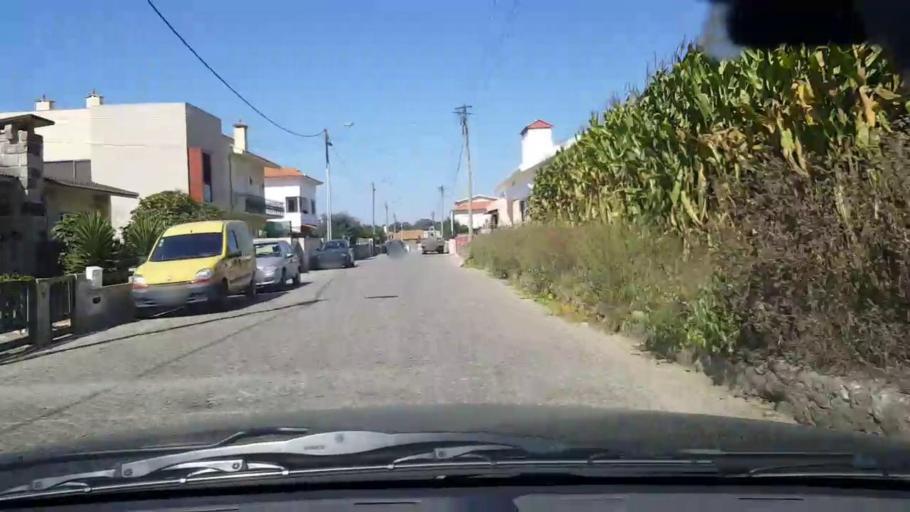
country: PT
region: Porto
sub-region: Matosinhos
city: Lavra
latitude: 41.2908
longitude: -8.7259
